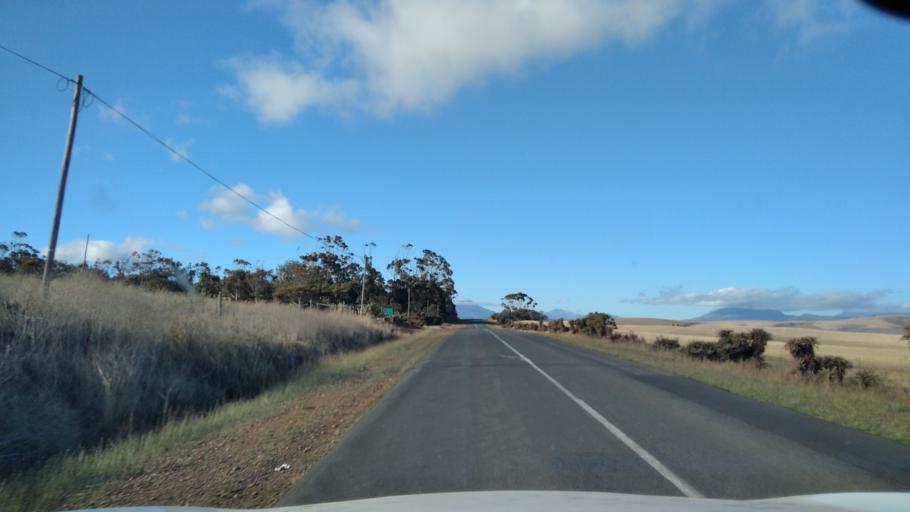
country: ZA
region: Western Cape
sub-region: Overberg District Municipality
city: Caledon
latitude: -34.2026
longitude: 19.2698
